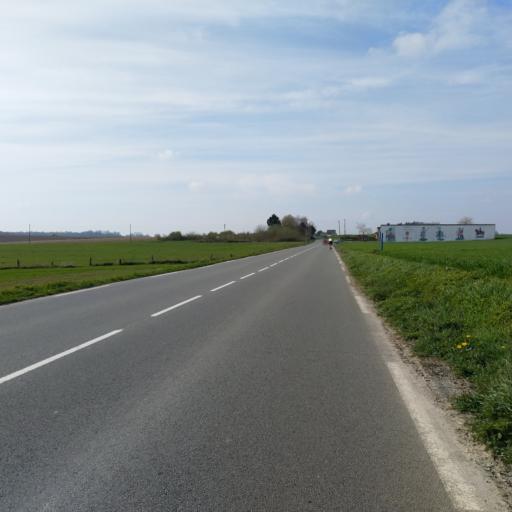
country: FR
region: Nord-Pas-de-Calais
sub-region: Departement du Nord
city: La Longueville
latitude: 50.3355
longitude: 3.8726
